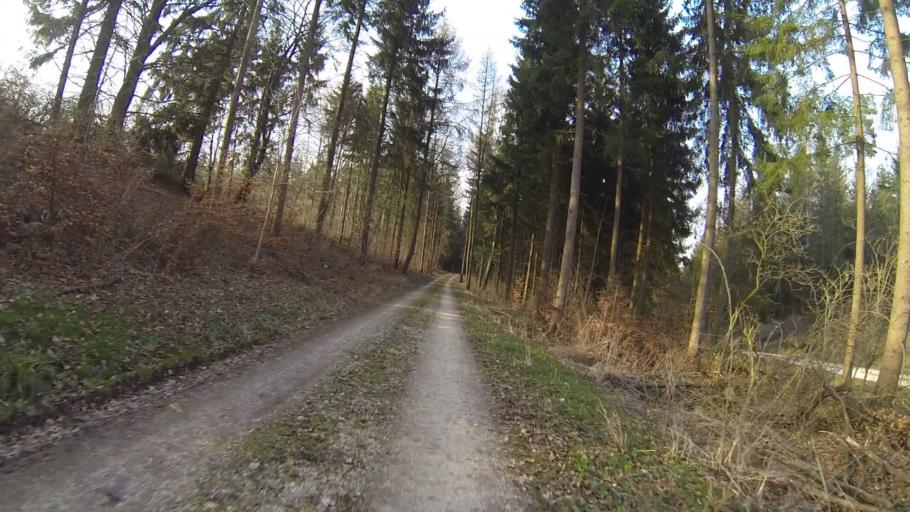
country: DE
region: Baden-Wuerttemberg
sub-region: Regierungsbezirk Stuttgart
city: Heidenheim an der Brenz
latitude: 48.6572
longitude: 10.1238
